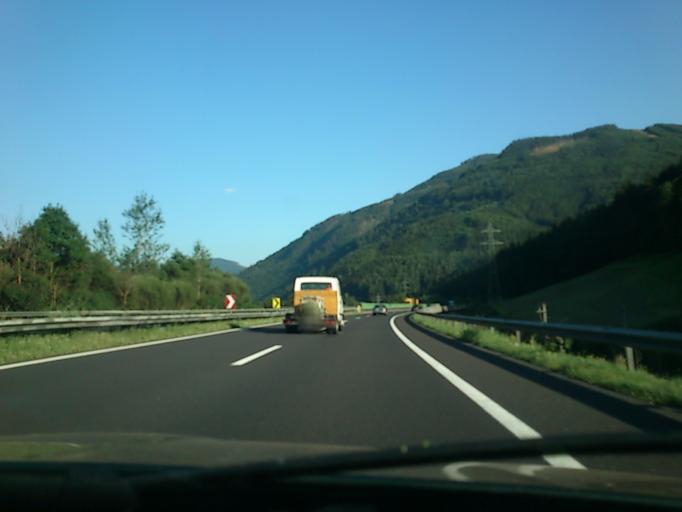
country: AT
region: Styria
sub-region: Politischer Bezirk Leoben
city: Kalwang
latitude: 47.4130
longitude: 14.7695
